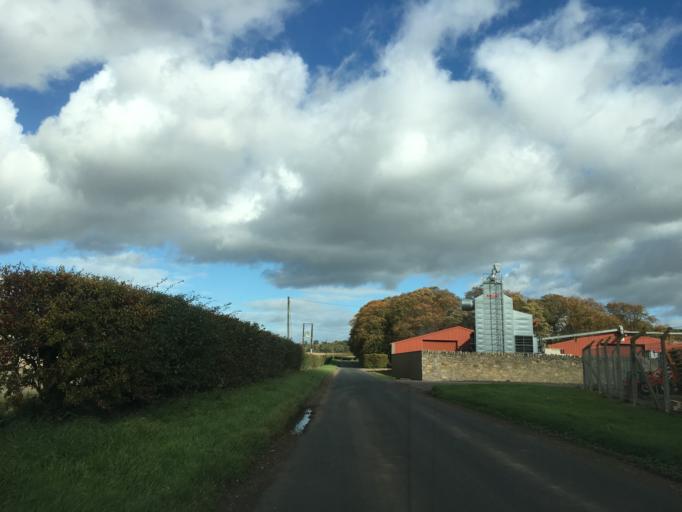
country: GB
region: Scotland
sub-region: East Lothian
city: Pencaitland
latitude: 55.8872
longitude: -2.9188
